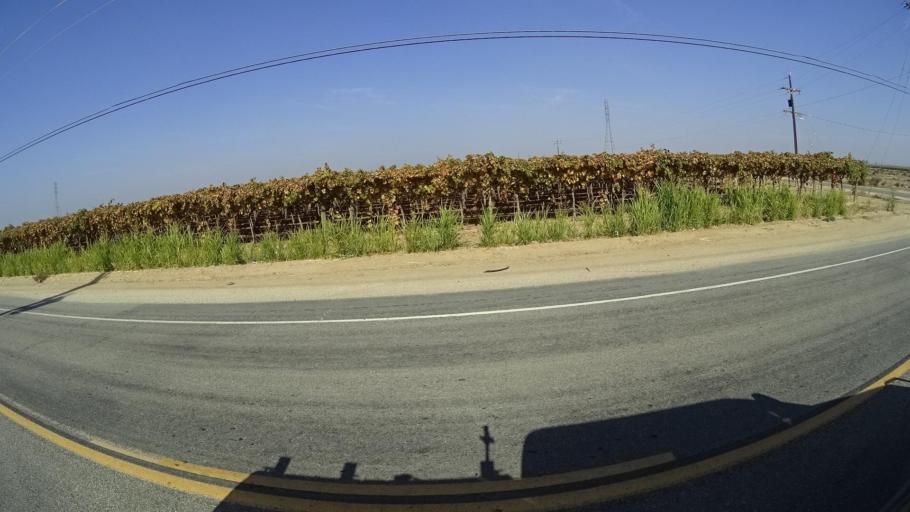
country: US
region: California
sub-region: Kern County
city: Greenacres
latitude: 35.4998
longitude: -119.1176
